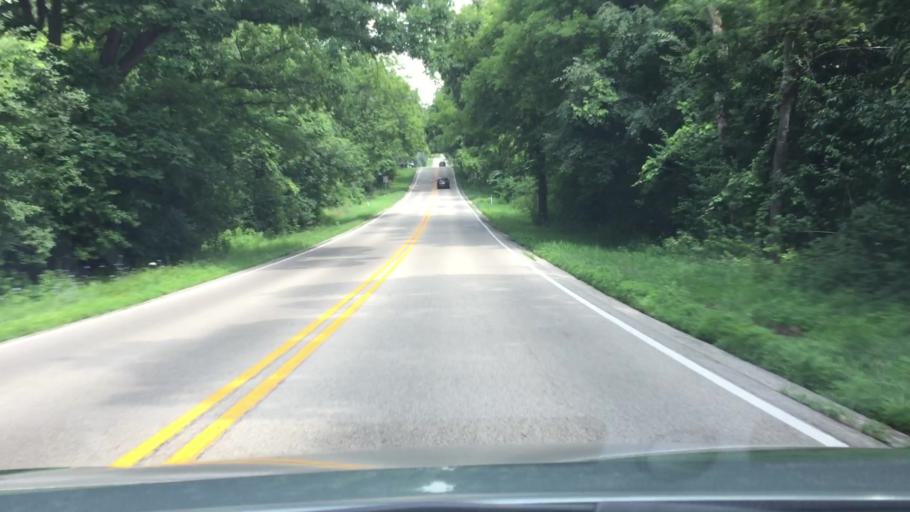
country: US
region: Wisconsin
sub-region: Waukesha County
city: Merton
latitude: 43.1279
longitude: -88.3078
